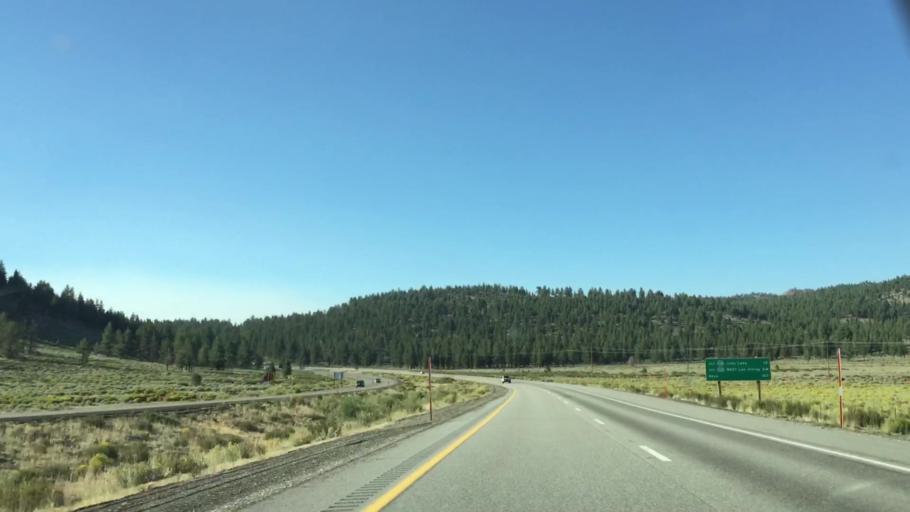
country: US
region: California
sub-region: Mono County
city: Mammoth Lakes
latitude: 37.6515
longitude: -118.9243
